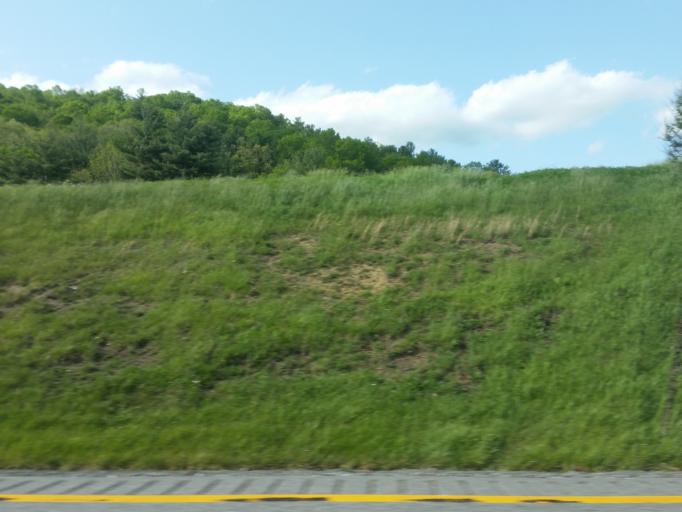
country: US
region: West Virginia
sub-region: Mercer County
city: Athens
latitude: 37.4929
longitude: -81.0948
